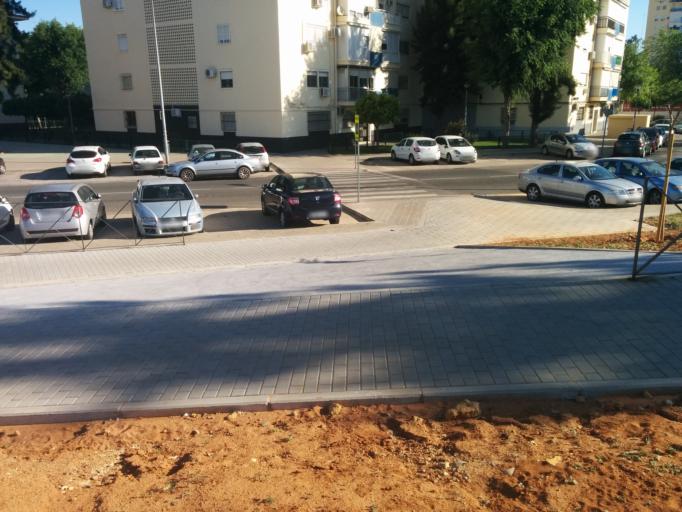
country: ES
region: Andalusia
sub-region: Provincia de Sevilla
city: Sevilla
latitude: 37.4067
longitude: -5.9219
